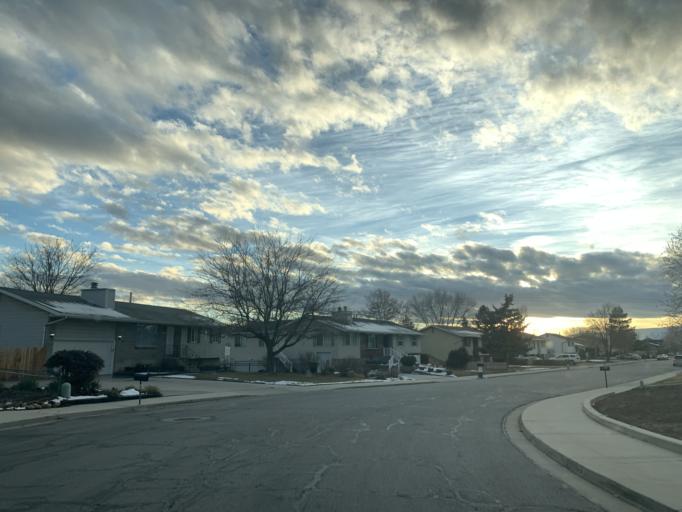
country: US
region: Utah
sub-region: Utah County
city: Provo
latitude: 40.2443
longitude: -111.6992
